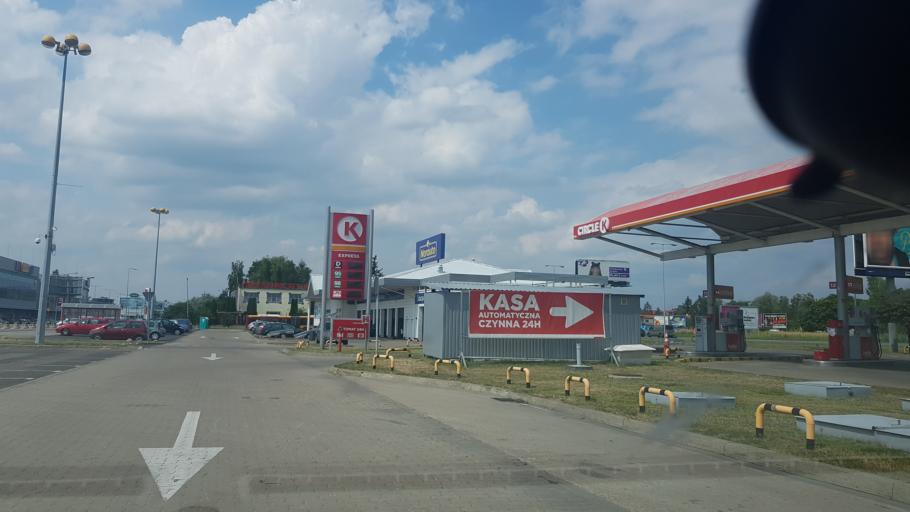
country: PL
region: Masovian Voivodeship
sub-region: Warszawa
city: Ursynow
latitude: 52.1421
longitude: 21.0238
